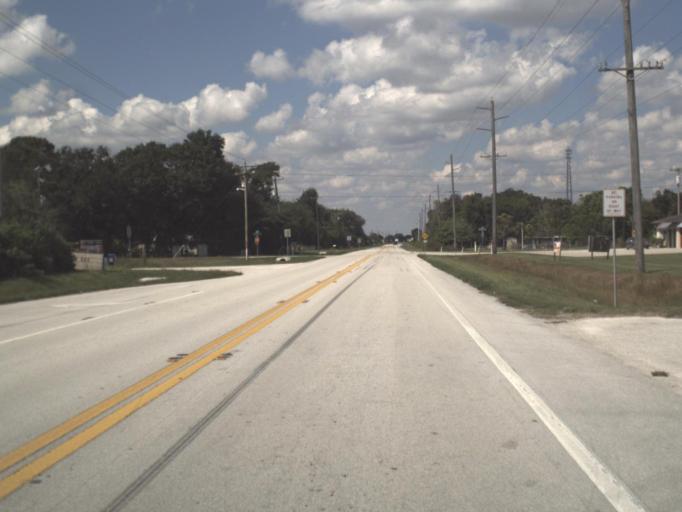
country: US
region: Florida
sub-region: Highlands County
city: Lake Placid
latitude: 27.4447
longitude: -81.2554
